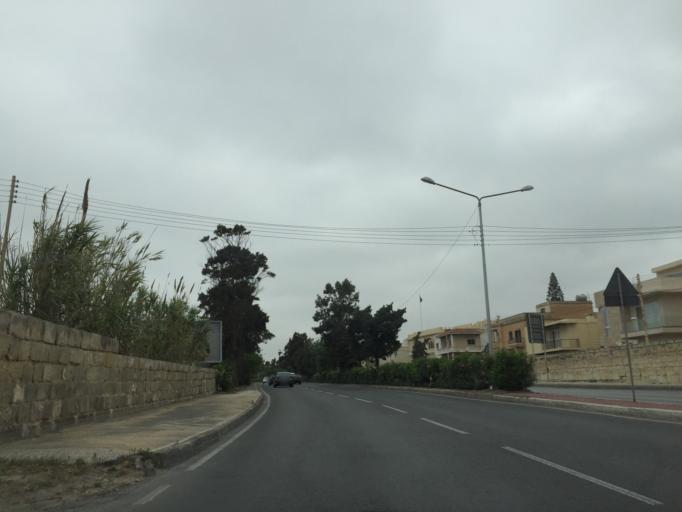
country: MT
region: Birkirkara
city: Birkirkara
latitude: 35.8930
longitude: 14.4559
